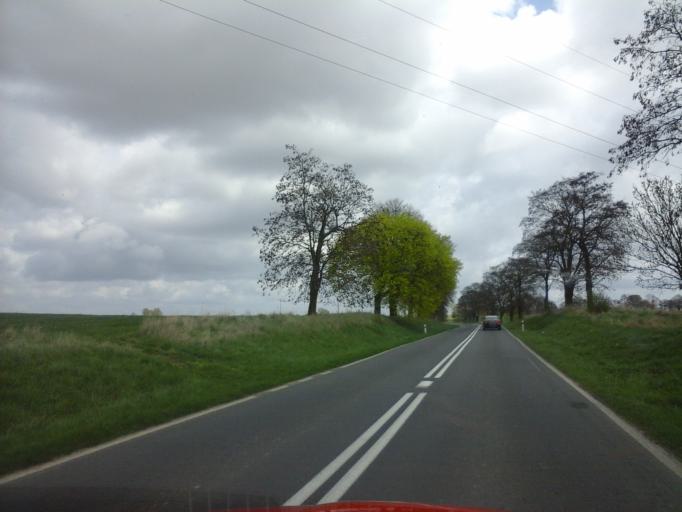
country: PL
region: West Pomeranian Voivodeship
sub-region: Powiat choszczenski
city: Krzecin
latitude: 53.1408
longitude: 15.5102
